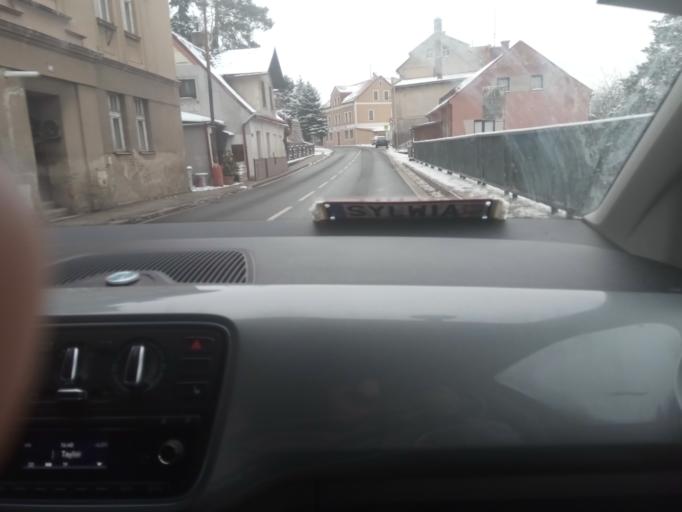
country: CZ
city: Jablonne v Podjestedi
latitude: 50.7649
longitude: 14.7584
